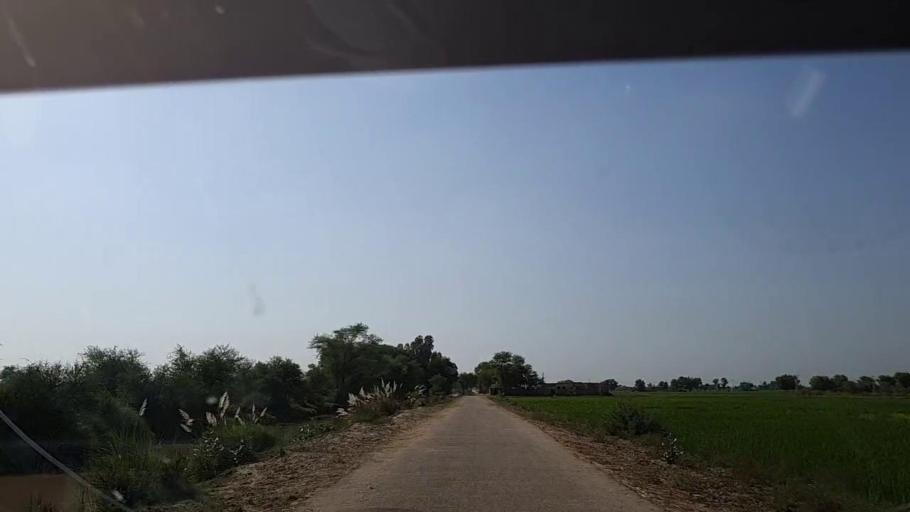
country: PK
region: Sindh
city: Tangwani
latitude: 28.2087
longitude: 69.0270
